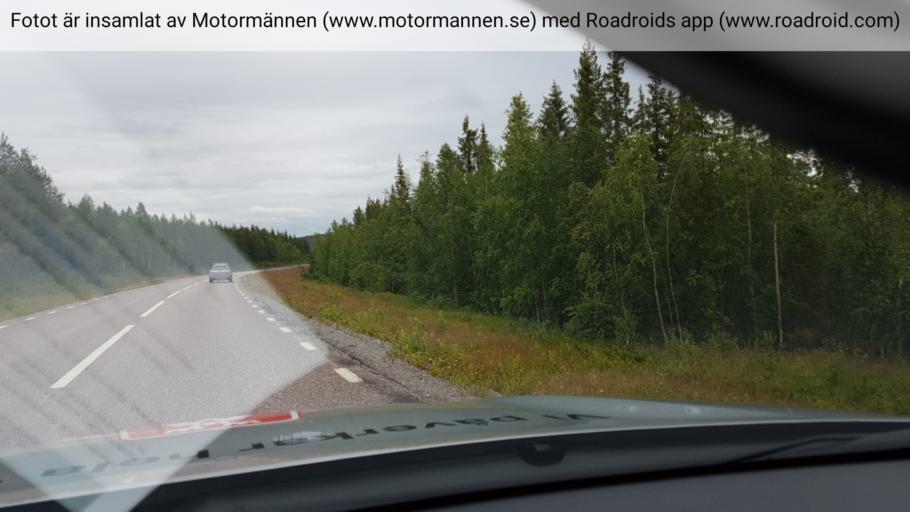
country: SE
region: Norrbotten
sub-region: Gallivare Kommun
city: Gaellivare
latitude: 67.0377
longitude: 21.6763
